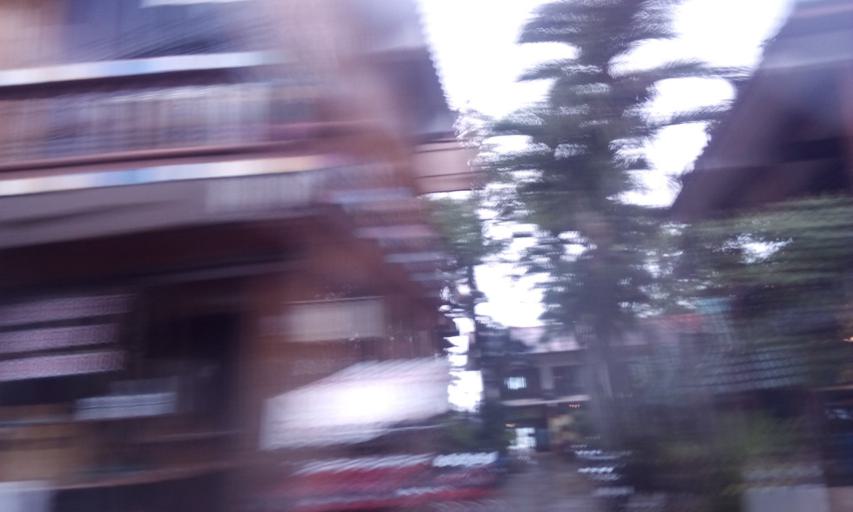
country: TH
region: Trat
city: Laem Ngop
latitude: 12.1031
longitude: 102.2738
